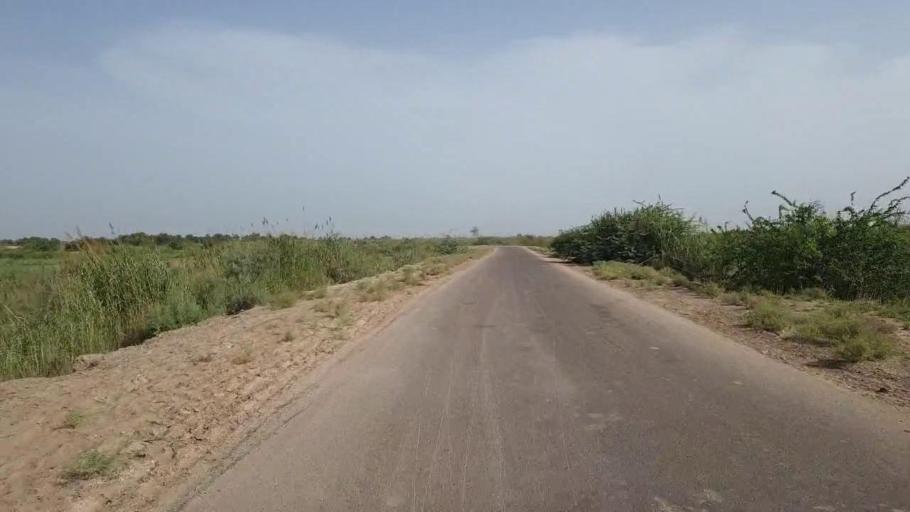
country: PK
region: Sindh
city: Sakrand
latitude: 26.2718
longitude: 68.2743
